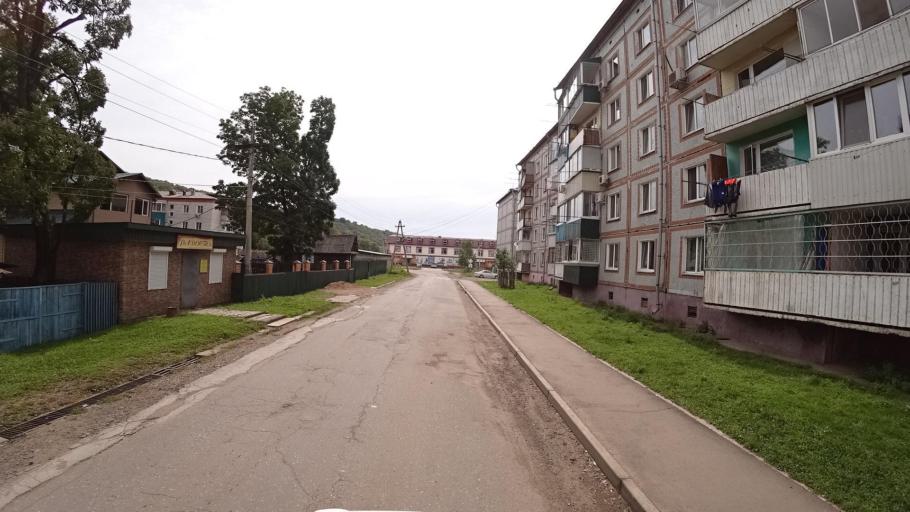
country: RU
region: Jewish Autonomous Oblast
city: Khingansk
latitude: 49.0099
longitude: 131.0546
